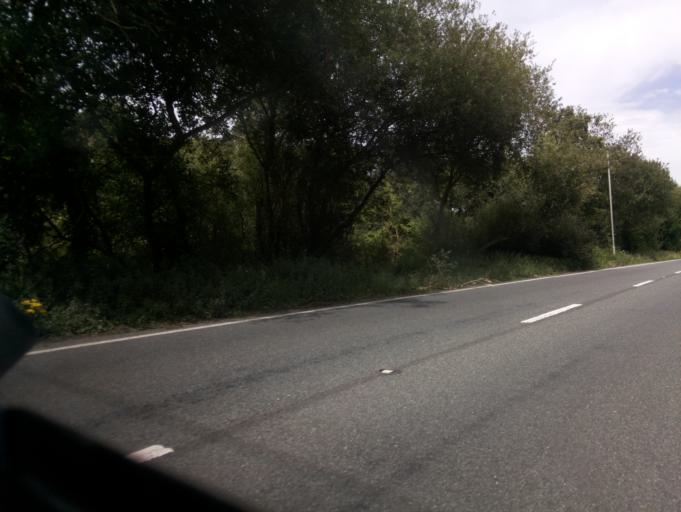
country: GB
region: England
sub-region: Somerset
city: Glastonbury
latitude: 51.1609
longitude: -2.7100
